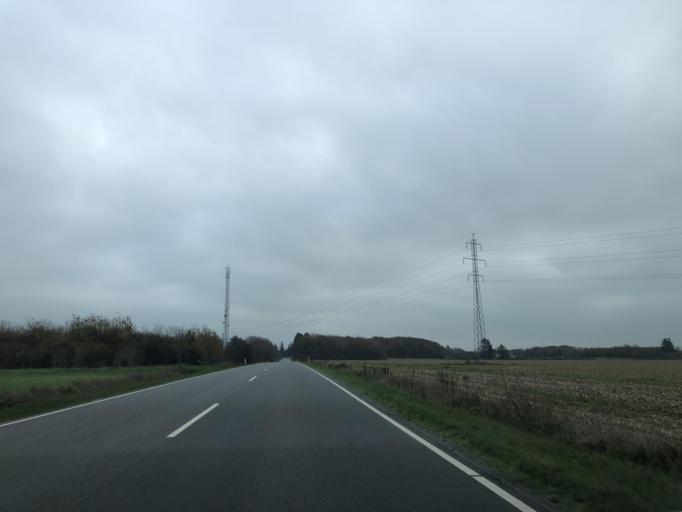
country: DK
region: South Denmark
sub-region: Haderslev Kommune
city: Gram
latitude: 55.2530
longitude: 8.9113
